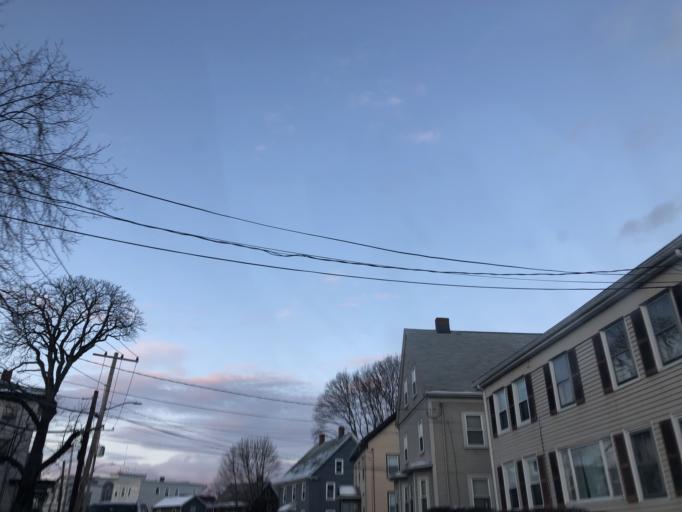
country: US
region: Massachusetts
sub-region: Middlesex County
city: Arlington
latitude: 42.4170
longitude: -71.1510
